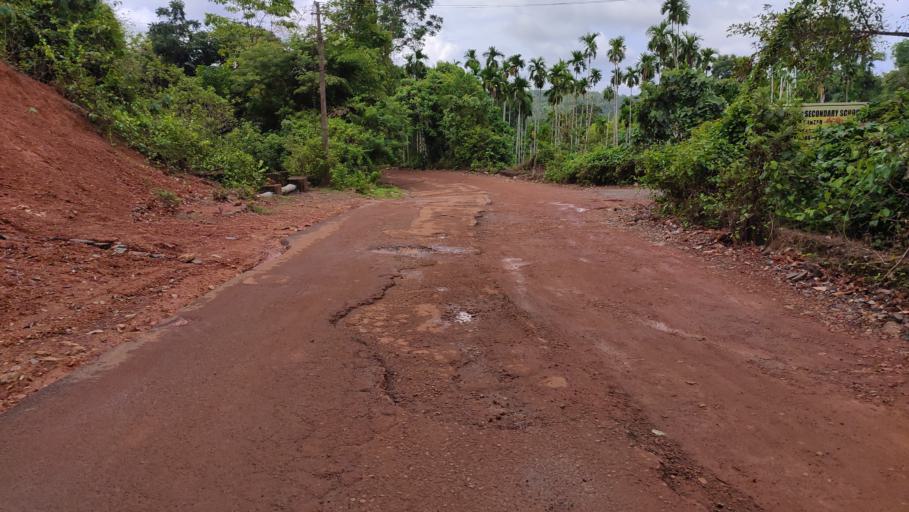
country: IN
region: Kerala
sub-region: Kasaragod District
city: Kasaragod
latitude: 12.5266
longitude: 75.0710
